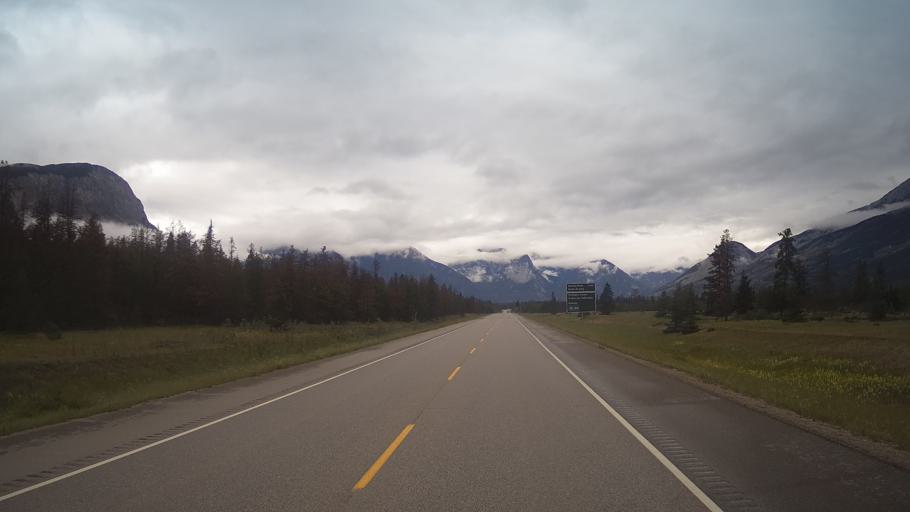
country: CA
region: Alberta
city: Jasper Park Lodge
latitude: 52.9541
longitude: -118.0442
